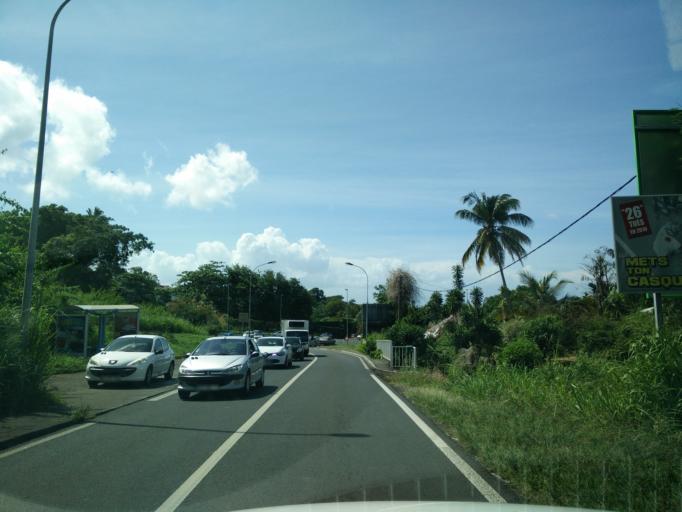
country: GP
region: Guadeloupe
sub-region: Guadeloupe
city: Basse-Terre
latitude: 15.9996
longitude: -61.7204
